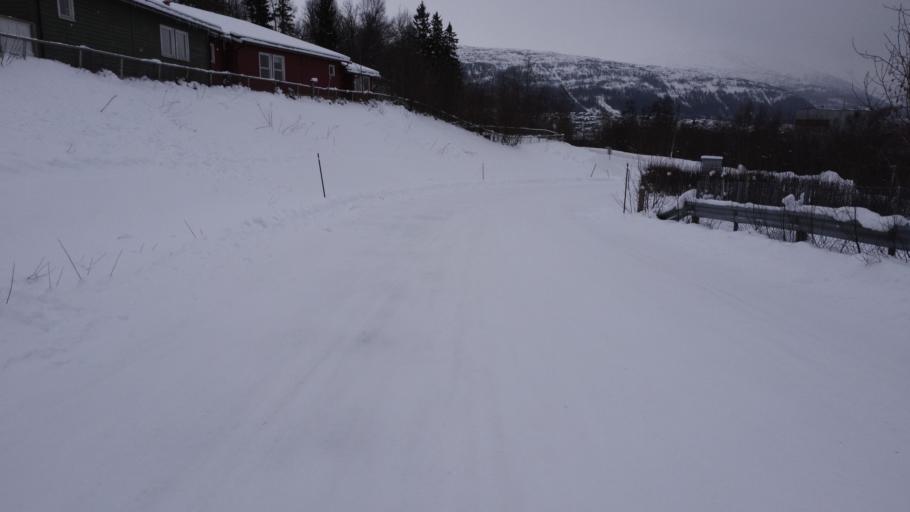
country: NO
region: Nordland
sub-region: Rana
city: Mo i Rana
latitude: 66.3291
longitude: 14.1545
